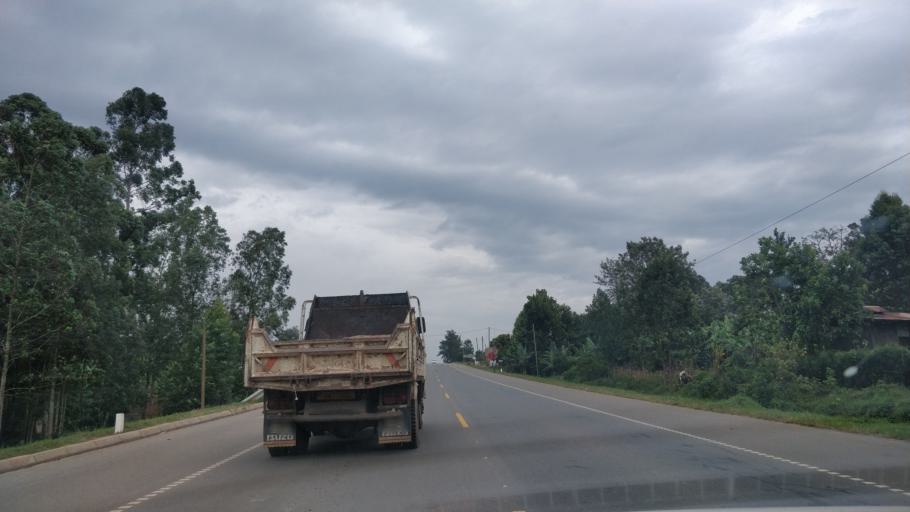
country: UG
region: Western Region
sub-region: Sheema District
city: Kibingo
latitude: -0.6589
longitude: 30.4627
